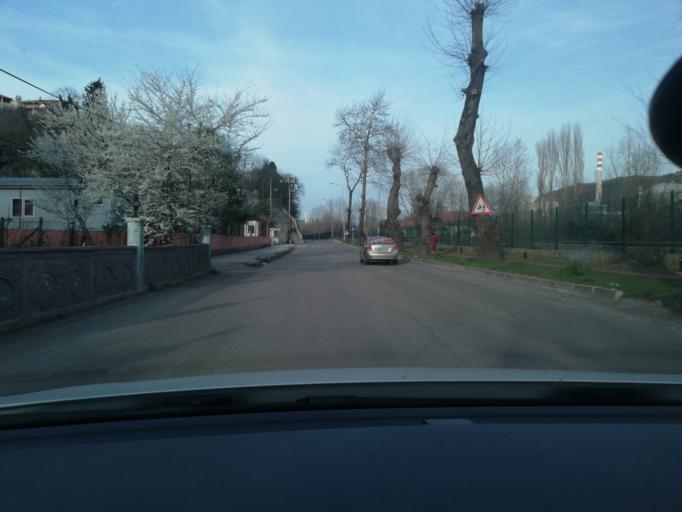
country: TR
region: Zonguldak
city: Kilimli
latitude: 41.5038
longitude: 31.8832
